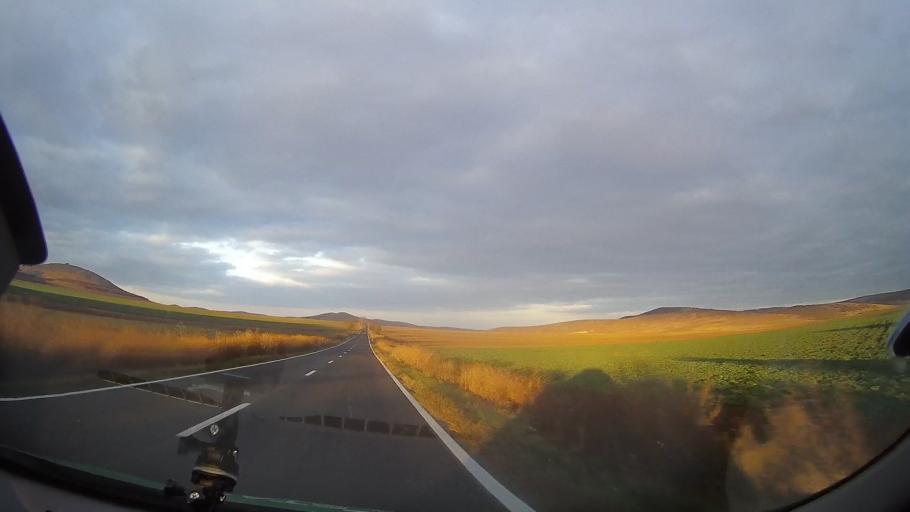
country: RO
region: Tulcea
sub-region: Comuna Nalbant
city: Nicolae Balcescu
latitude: 44.9716
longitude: 28.5403
